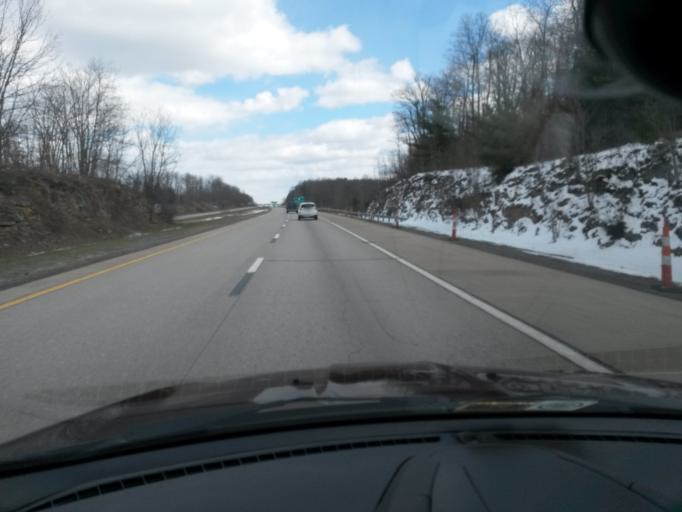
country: US
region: West Virginia
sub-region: Raleigh County
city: Daniels
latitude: 37.7737
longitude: -81.0850
